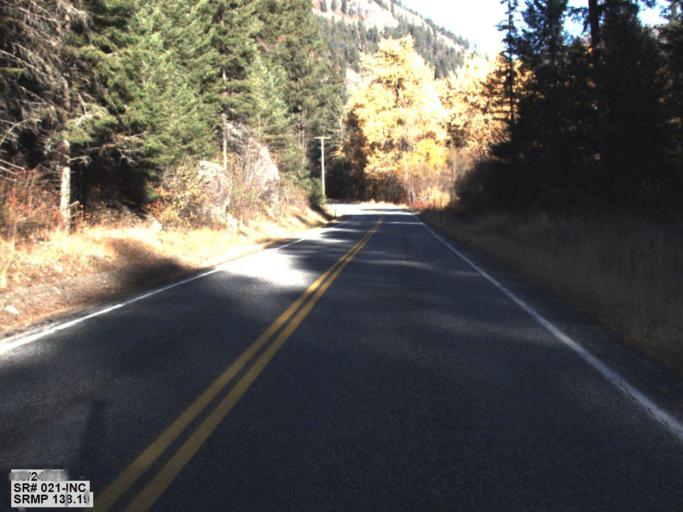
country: US
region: Washington
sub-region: Ferry County
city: Republic
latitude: 48.3646
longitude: -118.7437
